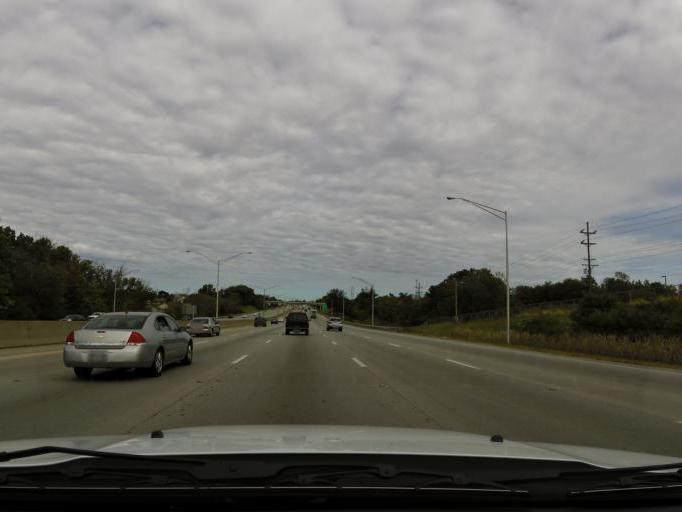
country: US
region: Kentucky
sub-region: Boone County
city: Florence
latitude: 38.9614
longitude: -84.6350
